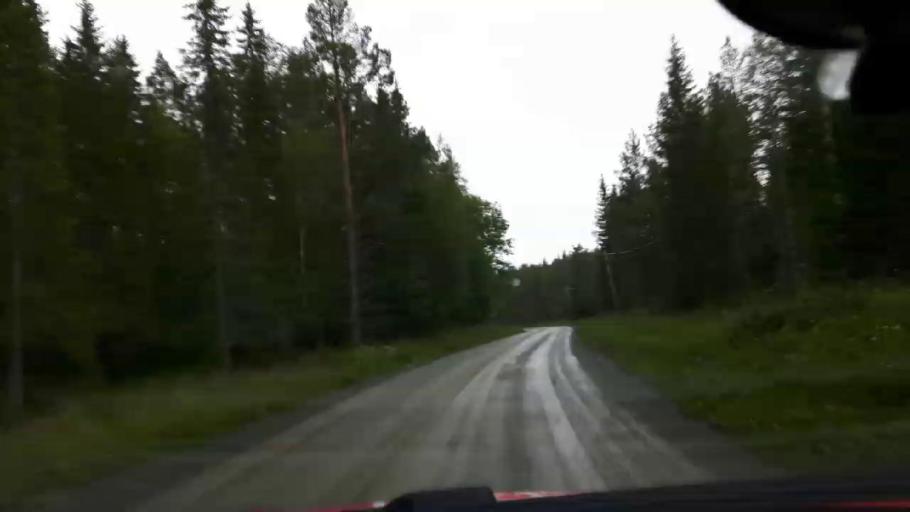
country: SE
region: Jaemtland
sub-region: OEstersunds Kommun
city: Brunflo
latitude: 62.8964
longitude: 14.8686
